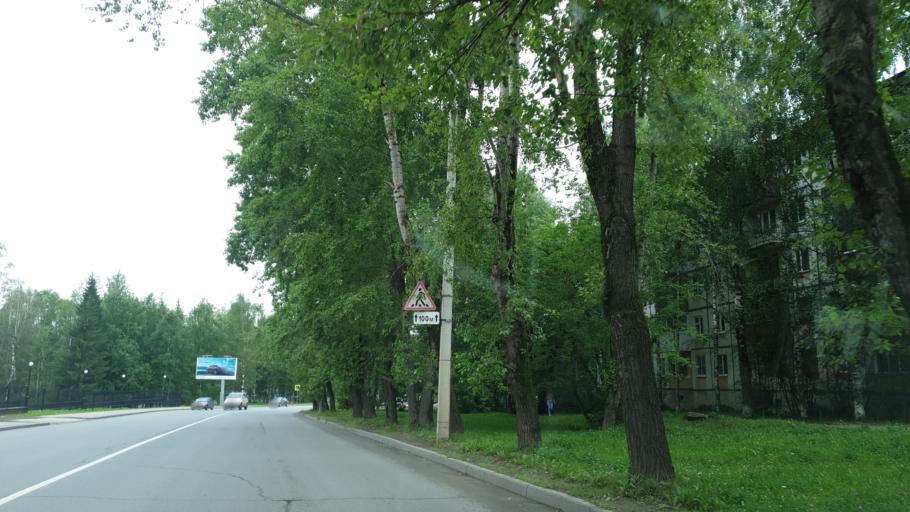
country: RU
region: Komi Republic
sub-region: Syktyvdinskiy Rayon
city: Syktyvkar
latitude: 61.6597
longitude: 50.8223
